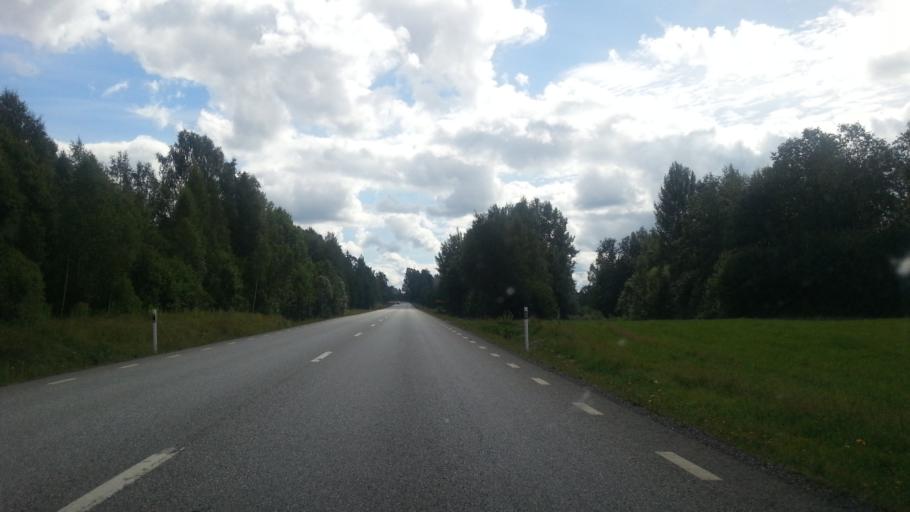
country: SE
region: OErebro
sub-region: Ljusnarsbergs Kommun
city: Kopparberg
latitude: 59.8439
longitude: 15.0760
